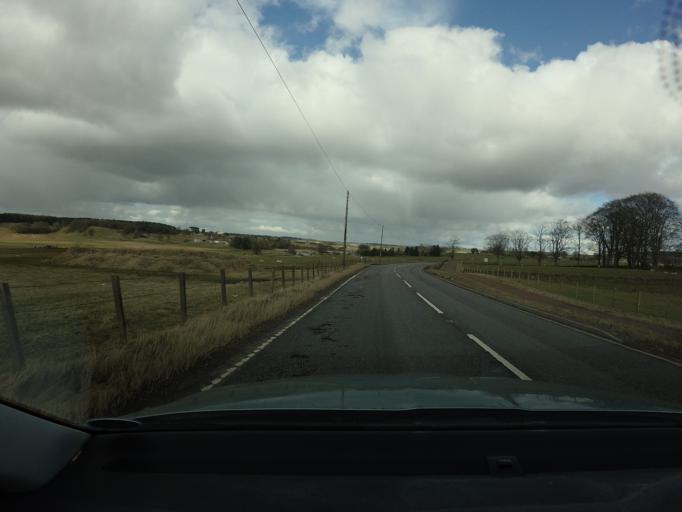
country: GB
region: Scotland
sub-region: South Lanarkshire
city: Lanark
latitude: 55.6488
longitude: -3.7314
